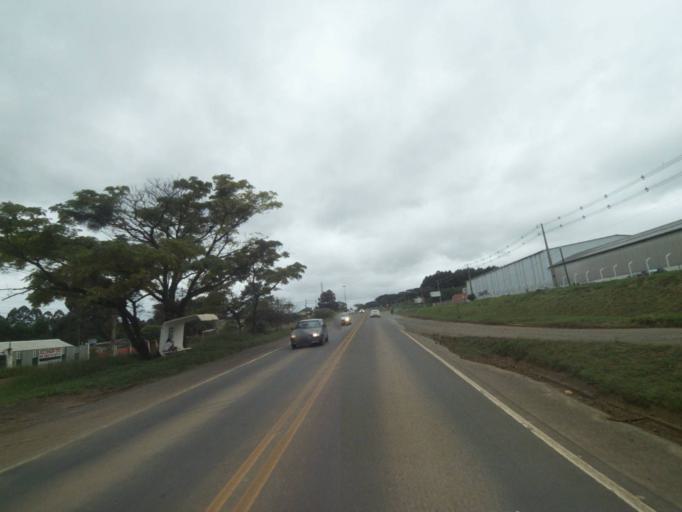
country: BR
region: Parana
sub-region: Telemaco Borba
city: Telemaco Borba
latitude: -24.3816
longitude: -50.6718
